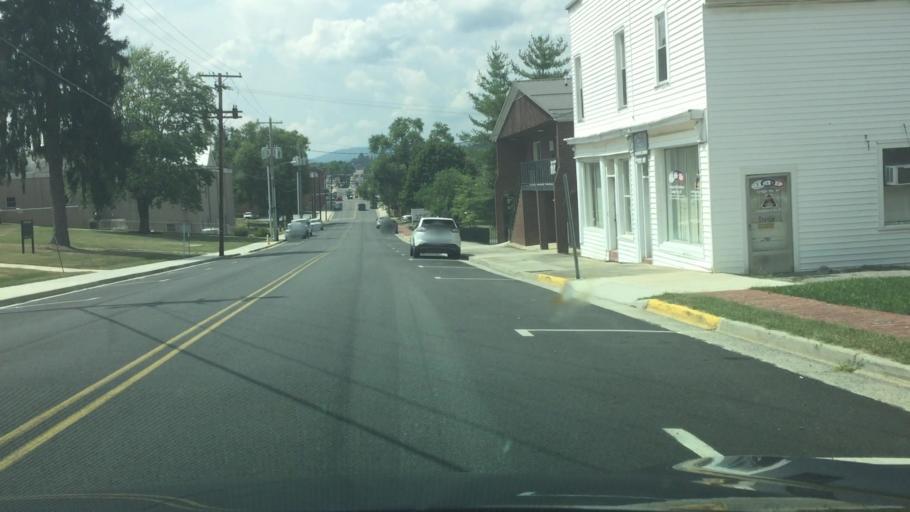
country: US
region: Virginia
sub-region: Wythe County
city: Wytheville
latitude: 36.9466
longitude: -81.0828
